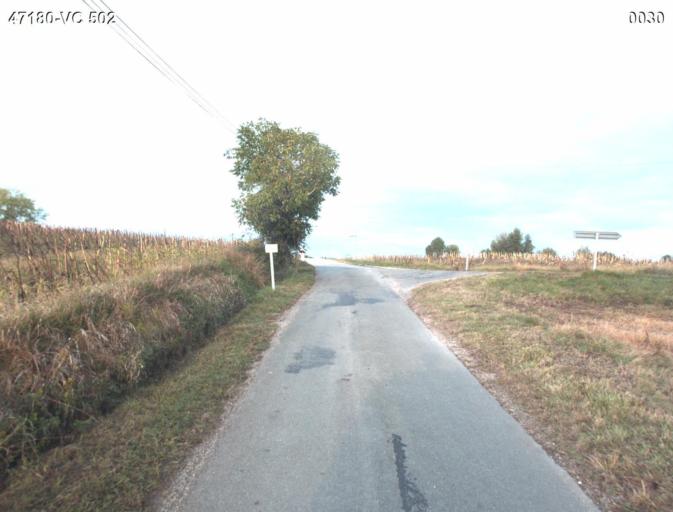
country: FR
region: Aquitaine
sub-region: Departement du Lot-et-Garonne
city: Sainte-Colombe-en-Bruilhois
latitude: 44.1619
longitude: 0.4750
